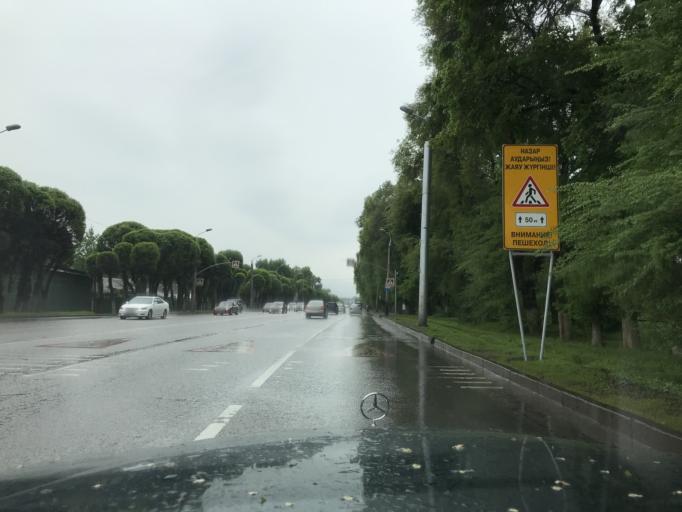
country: KZ
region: Almaty Qalasy
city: Almaty
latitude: 43.3042
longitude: 76.9530
